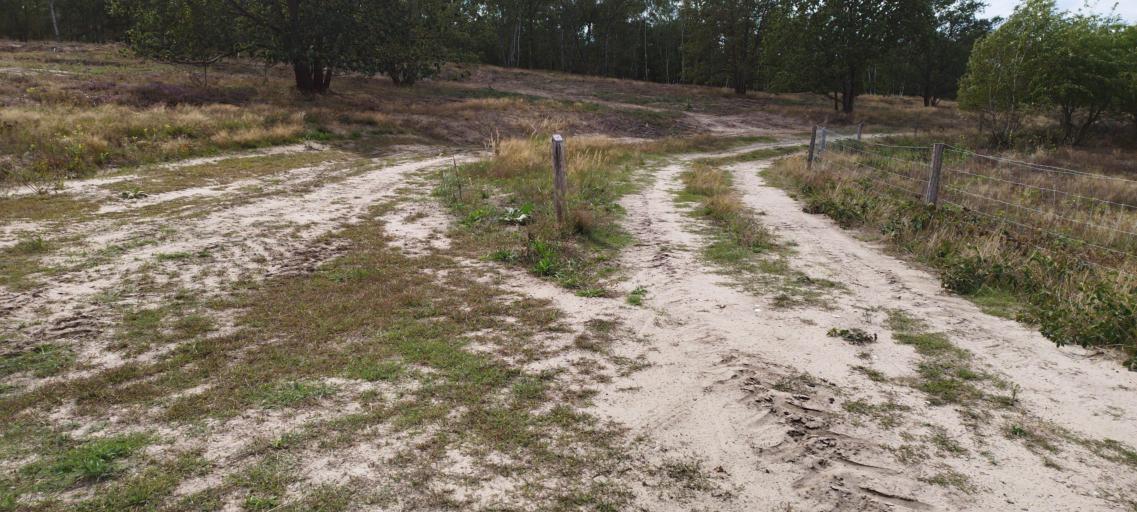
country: DE
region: Brandenburg
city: Dallgow-Doeberitz
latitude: 52.5183
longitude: 13.0078
